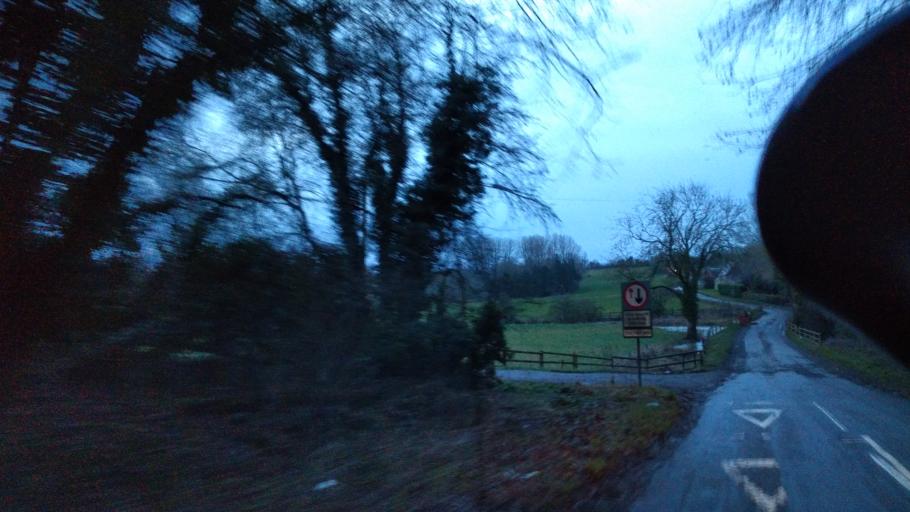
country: GB
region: England
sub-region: Oxfordshire
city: Shrivenham
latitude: 51.6142
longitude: -1.6814
